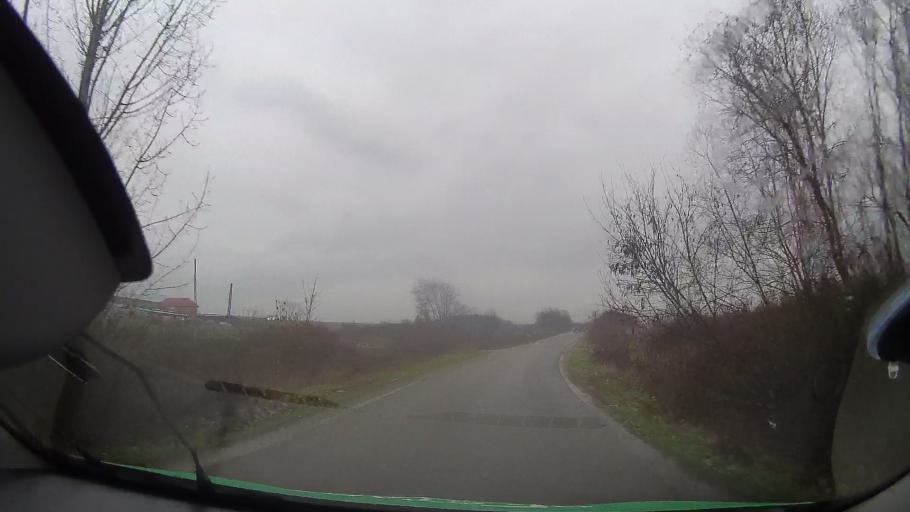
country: RO
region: Bihor
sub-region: Comuna Holod
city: Vintere
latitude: 46.7645
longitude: 22.1463
